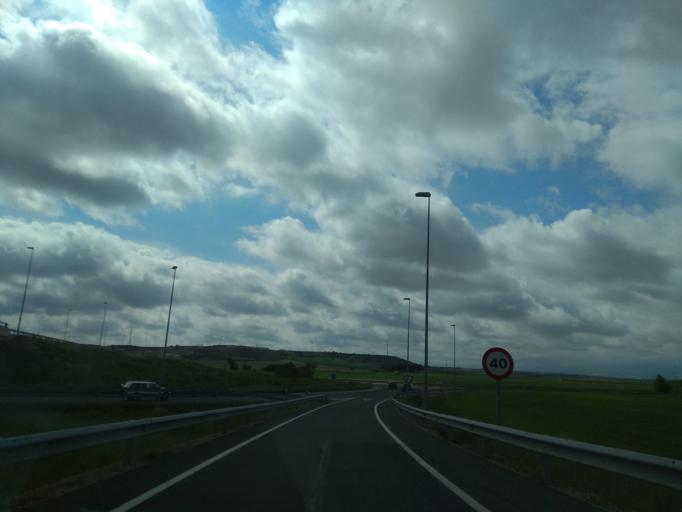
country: ES
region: La Rioja
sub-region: Provincia de La Rioja
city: Casalarreina
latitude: 42.5554
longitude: -2.8992
